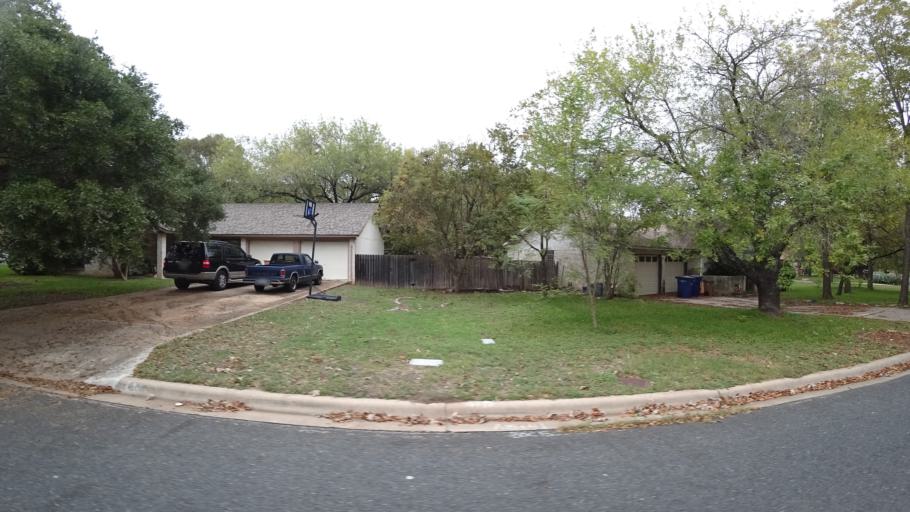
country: US
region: Texas
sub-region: Travis County
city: Barton Creek
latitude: 30.2360
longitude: -97.8868
